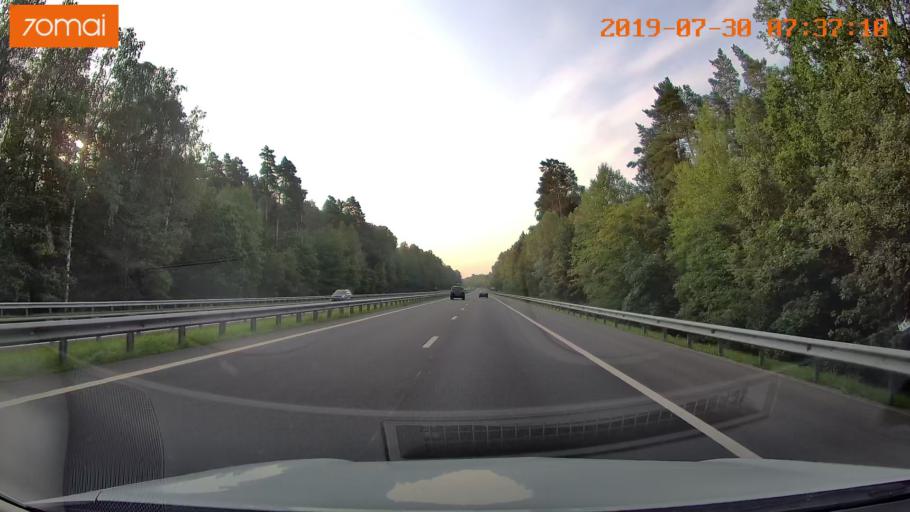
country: RU
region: Kaliningrad
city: Gvardeysk
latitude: 54.6579
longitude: 21.1410
